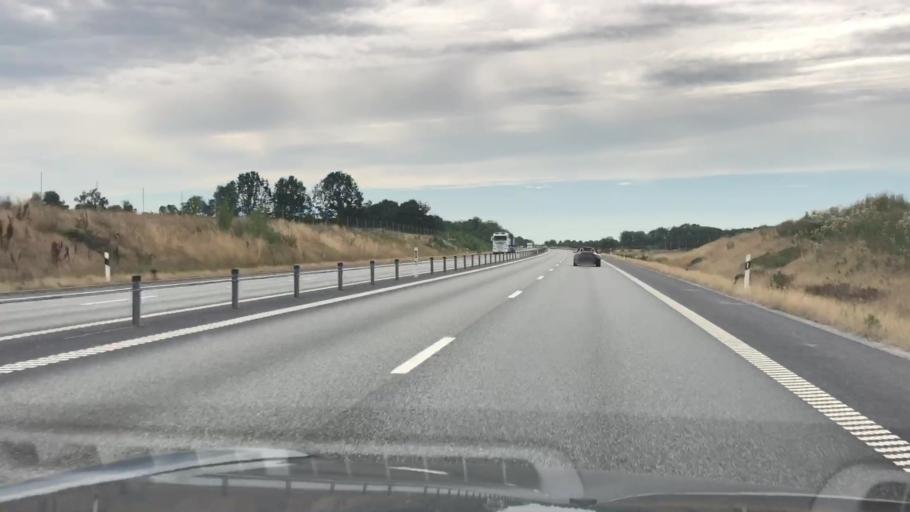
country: SE
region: Blekinge
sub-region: Karlshamns Kommun
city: Morrum
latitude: 56.1554
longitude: 14.6654
